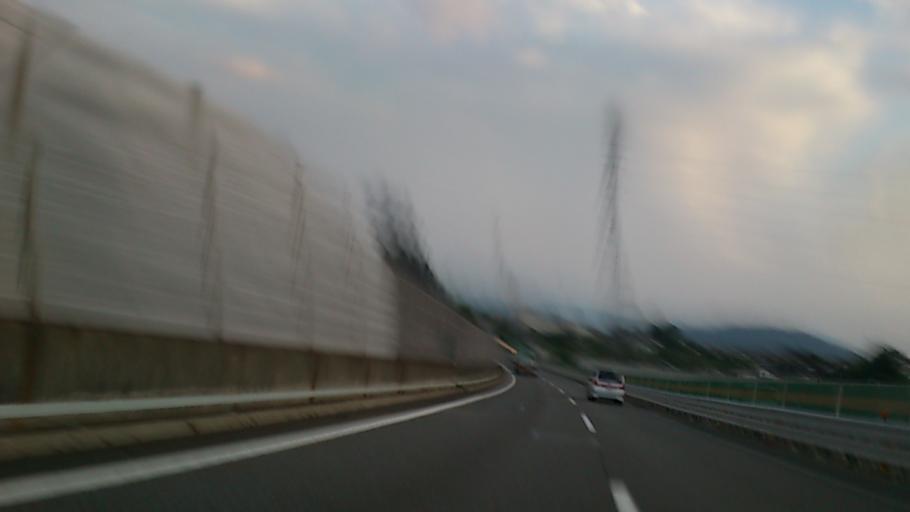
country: JP
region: Nagano
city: Iida
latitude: 35.5157
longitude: 137.8027
